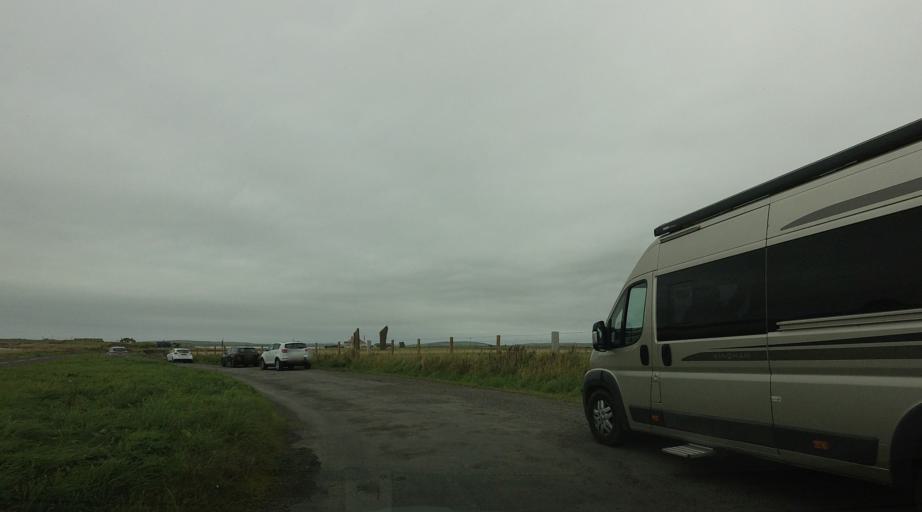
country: GB
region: Scotland
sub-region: Orkney Islands
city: Stromness
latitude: 58.9929
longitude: -3.2076
